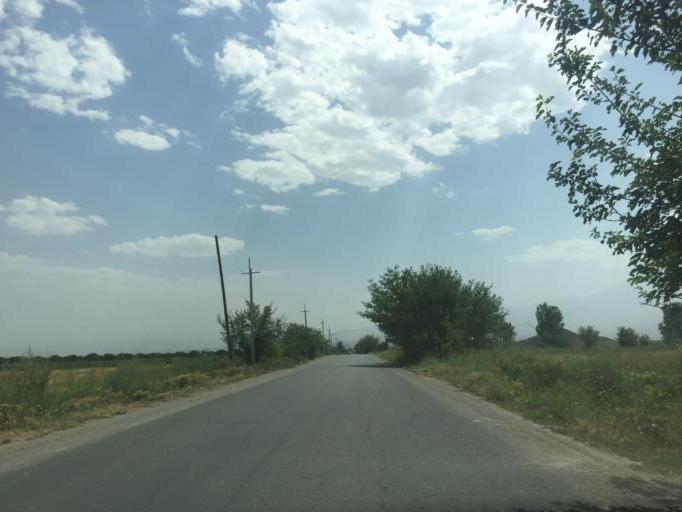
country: AM
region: Ararat
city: Shahumyan
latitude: 39.8856
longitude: 44.5919
